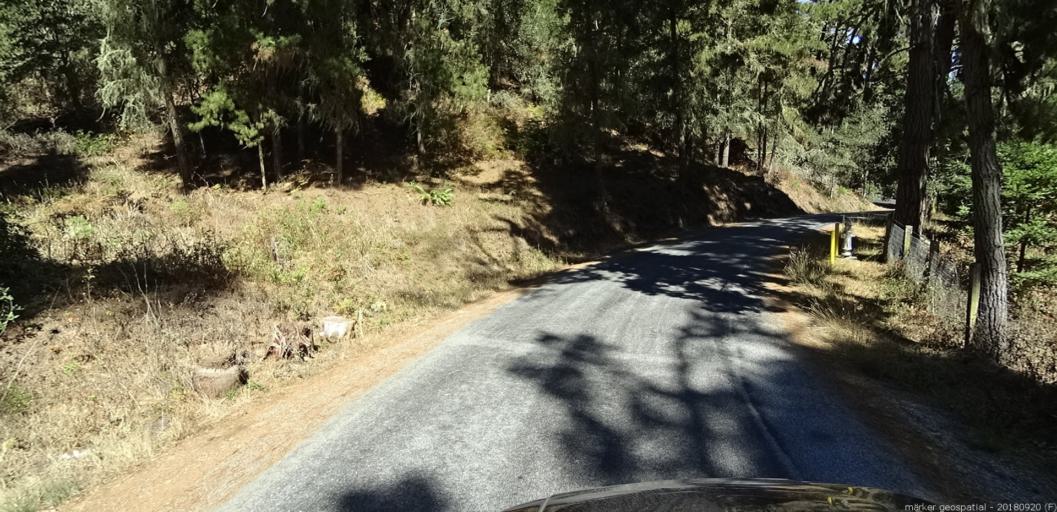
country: US
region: California
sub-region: Monterey County
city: Carmel-by-the-Sea
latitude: 36.5733
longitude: -121.9026
